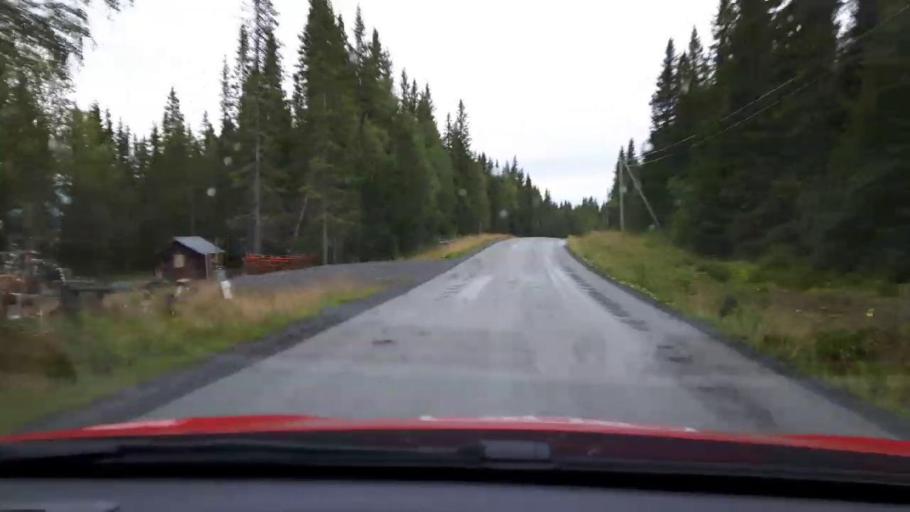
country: SE
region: Jaemtland
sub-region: Are Kommun
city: Are
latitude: 63.4635
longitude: 13.1908
